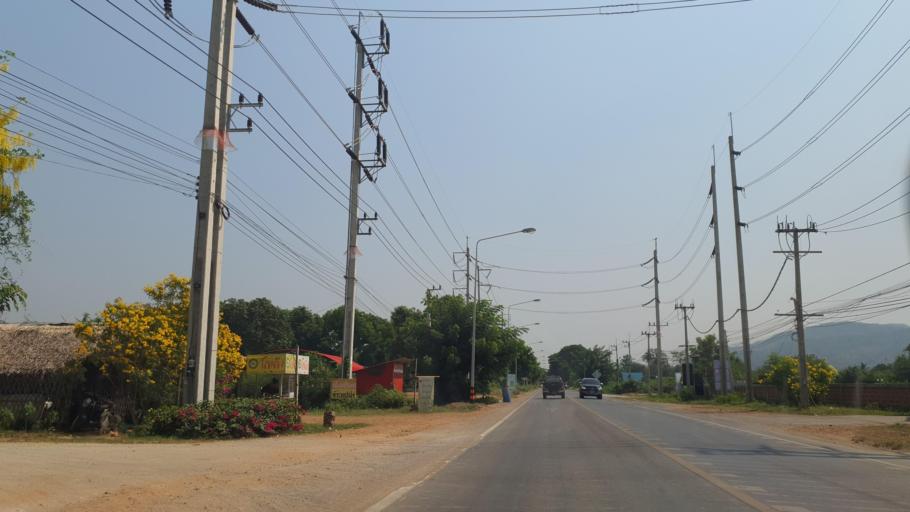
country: TH
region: Kanchanaburi
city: Kanchanaburi
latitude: 14.0557
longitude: 99.4753
